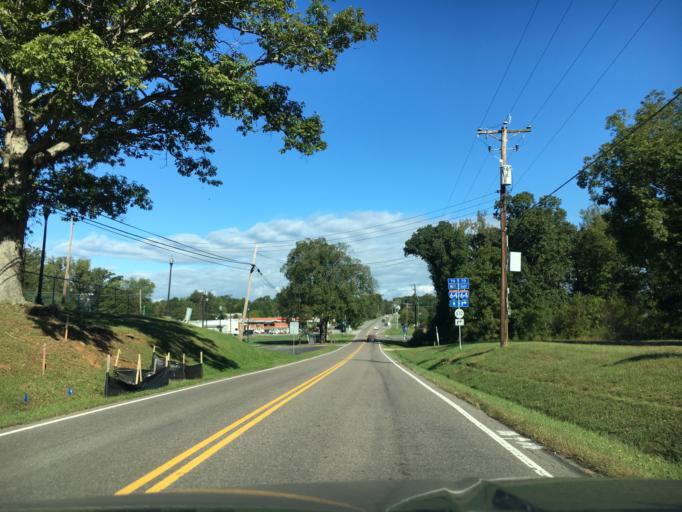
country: US
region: Virginia
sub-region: Goochland County
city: Goochland
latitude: 37.6964
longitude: -77.8878
